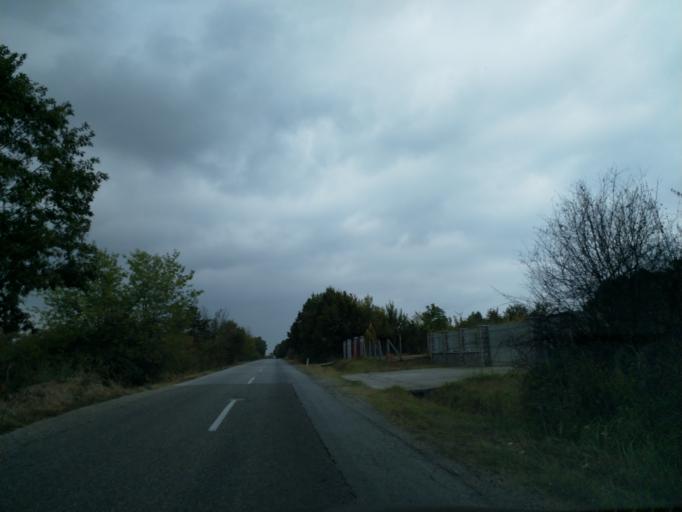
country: RS
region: Central Serbia
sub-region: Pomoravski Okrug
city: Jagodina
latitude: 44.0126
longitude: 21.2004
